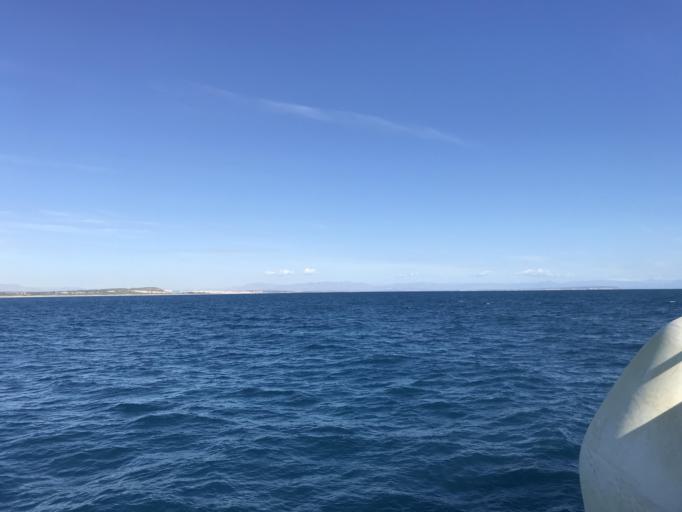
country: ES
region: Valencia
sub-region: Provincia de Alicante
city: Torrevieja
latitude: 38.0100
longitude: -0.6299
